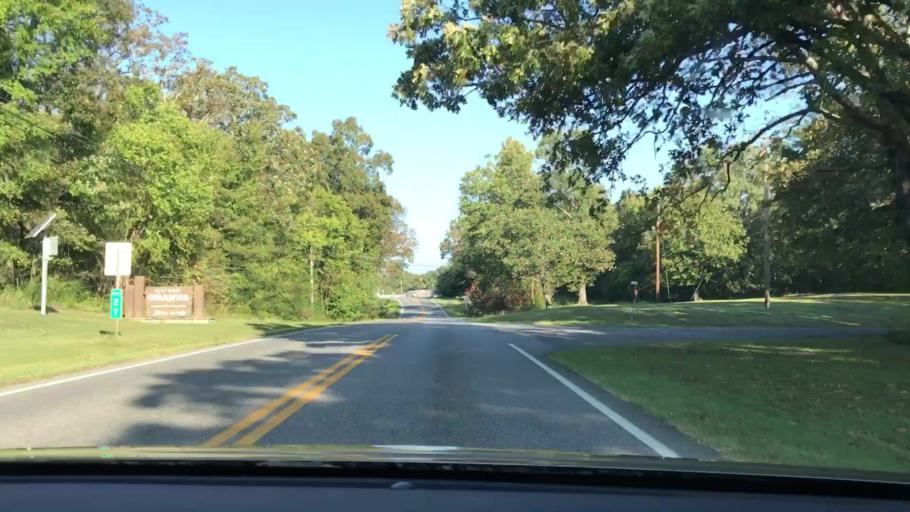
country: US
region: Kentucky
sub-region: Marshall County
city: Benton
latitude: 36.7728
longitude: -88.1392
